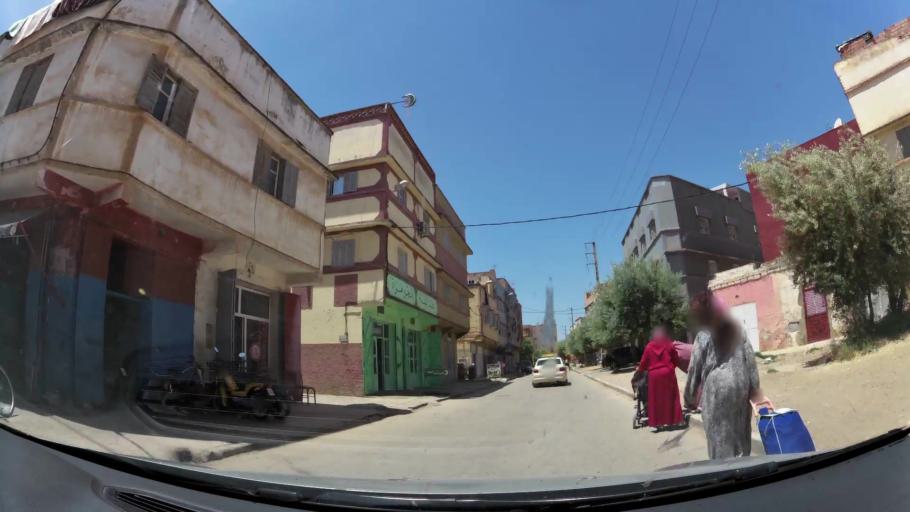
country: MA
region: Rabat-Sale-Zemmour-Zaer
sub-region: Khemisset
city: Khemisset
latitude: 33.8284
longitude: -6.0755
